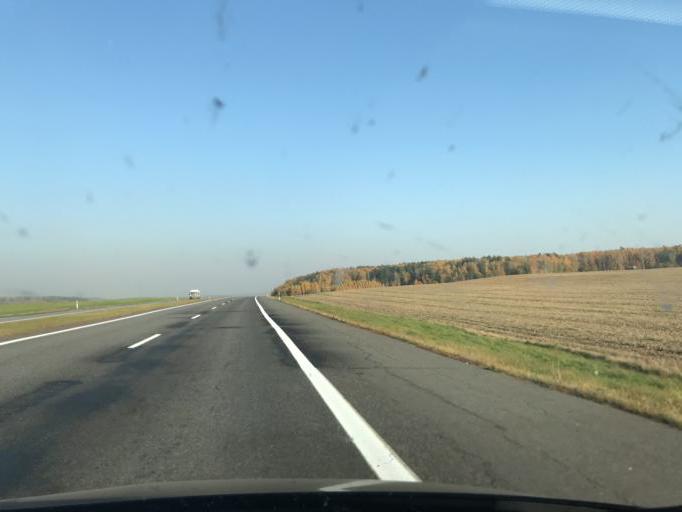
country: BY
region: Brest
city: Haradzishcha
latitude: 53.2370
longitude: 26.1812
